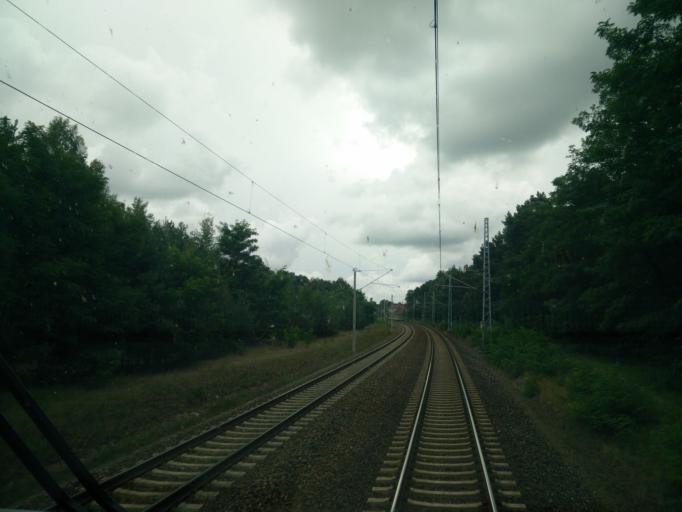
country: DE
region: Brandenburg
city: Gross Koris
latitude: 52.1634
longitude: 13.6490
